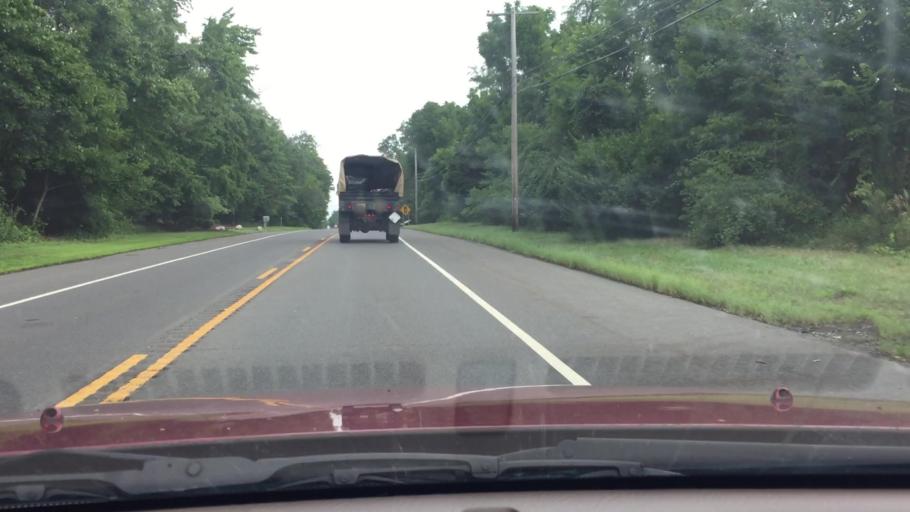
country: US
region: New Jersey
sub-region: Burlington County
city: Fort Dix
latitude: 40.0526
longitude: -74.6485
